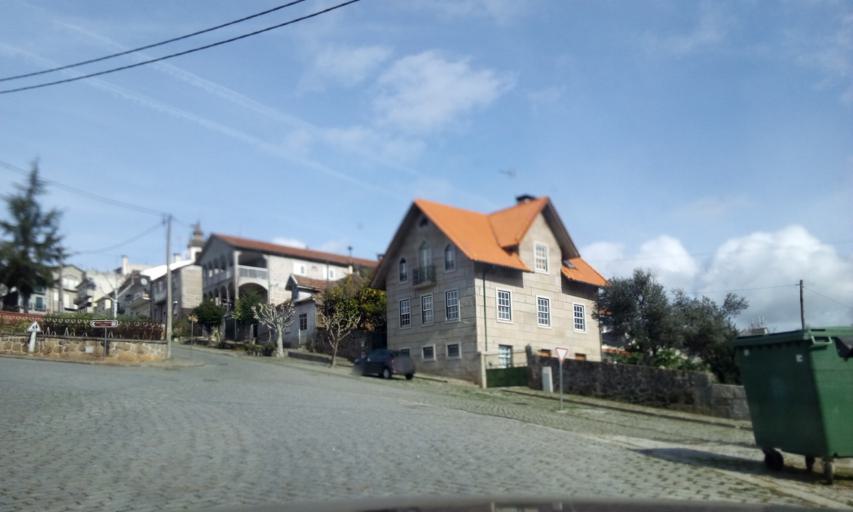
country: PT
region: Viseu
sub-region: Satao
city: Satao
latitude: 40.6727
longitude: -7.6991
